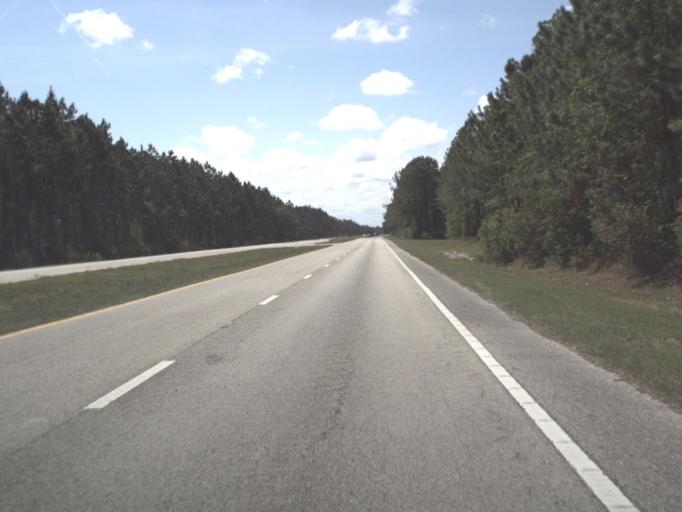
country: US
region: Florida
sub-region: Flagler County
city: Palm Coast
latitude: 29.6326
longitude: -81.2841
